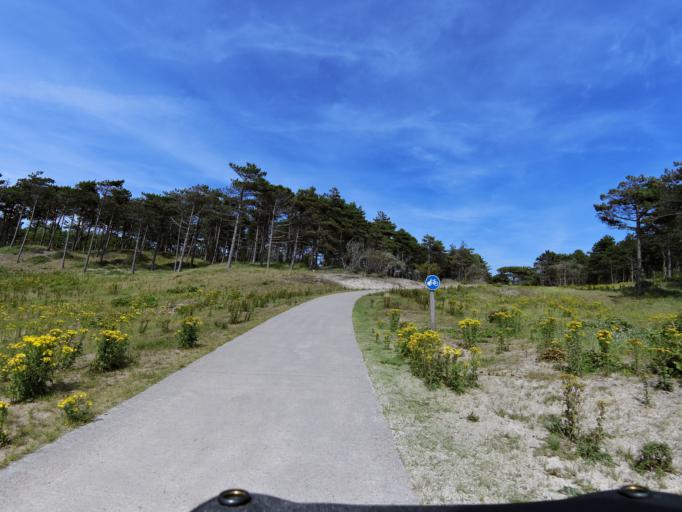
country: NL
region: Zeeland
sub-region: Schouwen-Duiveland
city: Burgh
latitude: 51.6831
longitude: 3.6895
